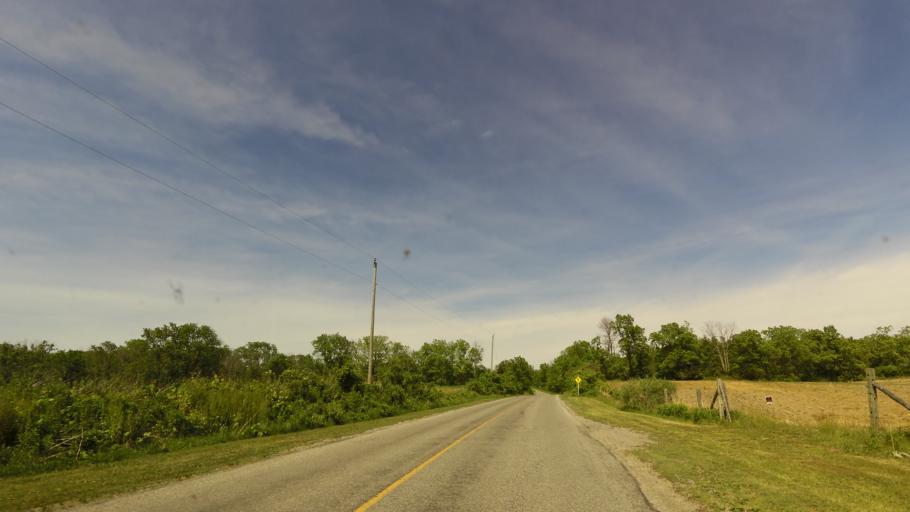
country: CA
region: Ontario
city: Norfolk County
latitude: 42.7302
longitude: -80.2901
